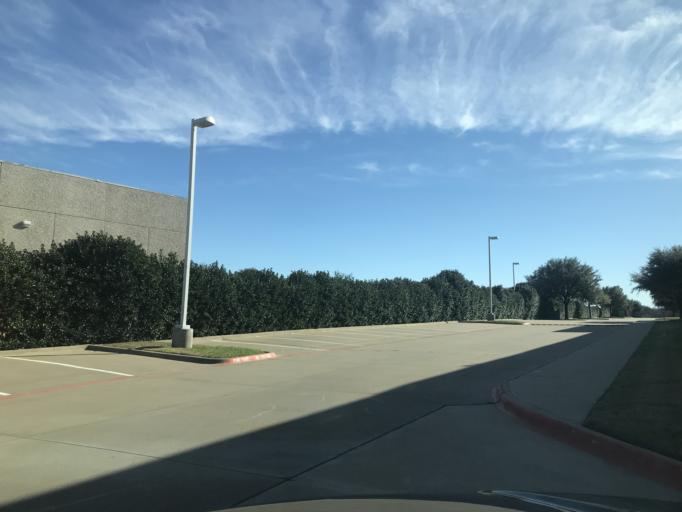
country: US
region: Texas
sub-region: Tarrant County
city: Haltom City
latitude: 32.8185
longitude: -97.3102
